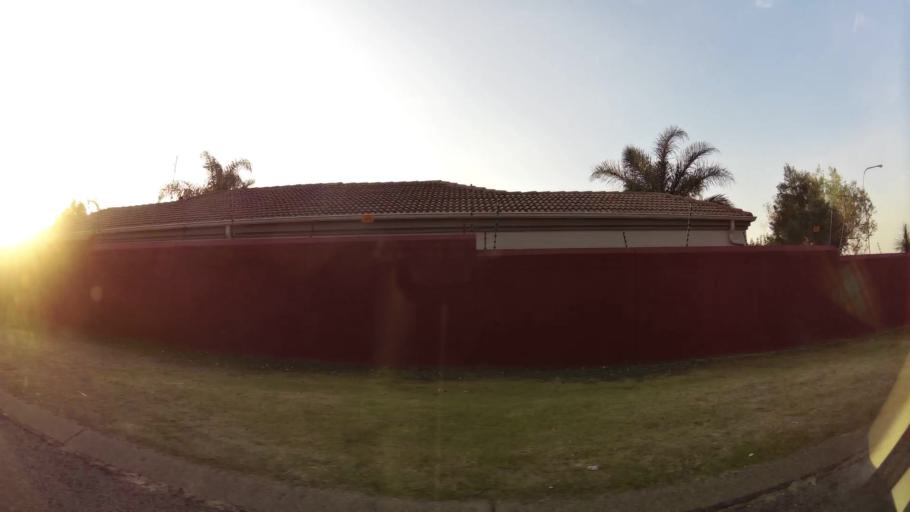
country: ZA
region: Gauteng
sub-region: City of Johannesburg Metropolitan Municipality
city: Modderfontein
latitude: -26.0866
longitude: 28.2183
